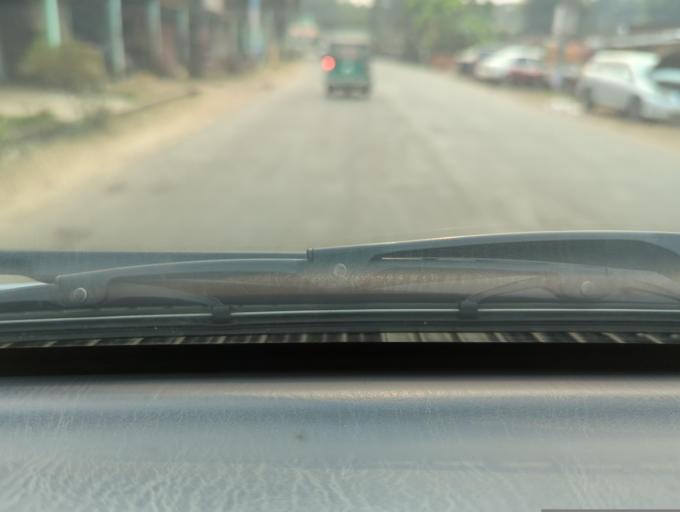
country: BD
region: Sylhet
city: Maulavi Bazar
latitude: 24.4916
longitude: 91.7473
